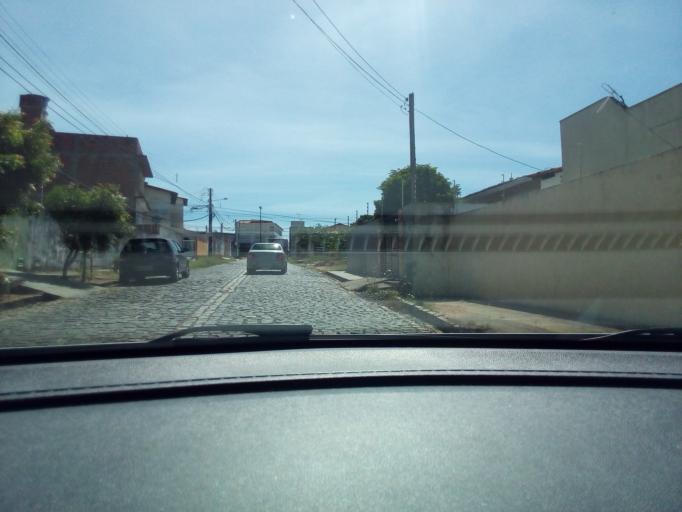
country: BR
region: Rio Grande do Norte
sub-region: Parnamirim
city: Parnamirim
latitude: -5.8896
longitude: -35.1936
